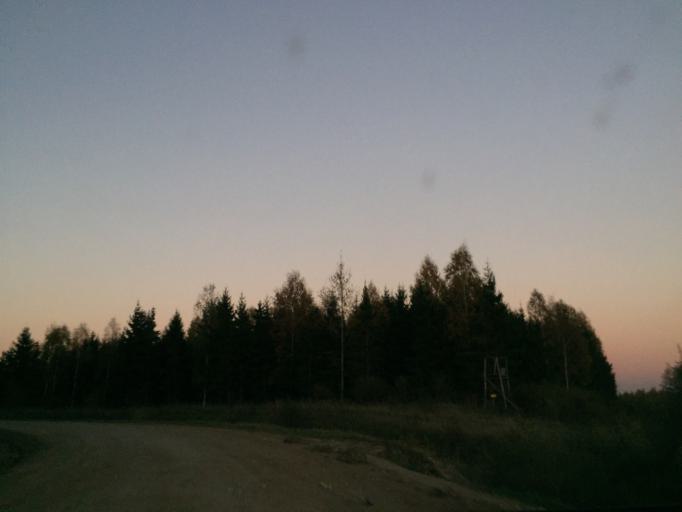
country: LV
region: Auces Novads
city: Auce
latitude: 56.4069
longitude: 22.7985
